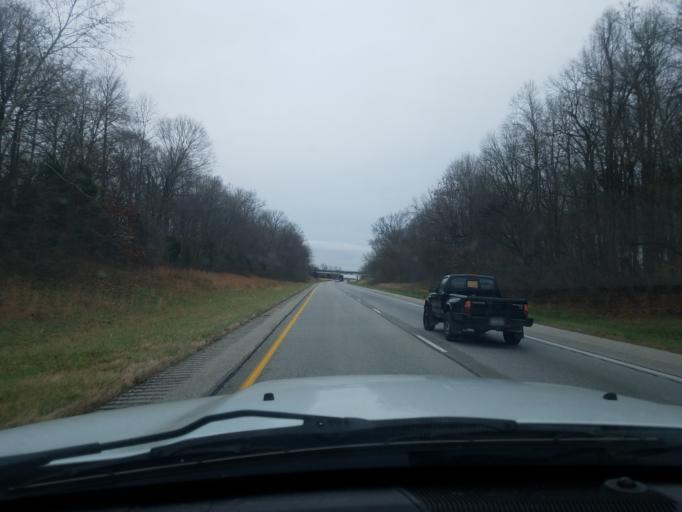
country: US
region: Indiana
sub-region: Harrison County
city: Corydon
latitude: 38.2502
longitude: -86.0550
